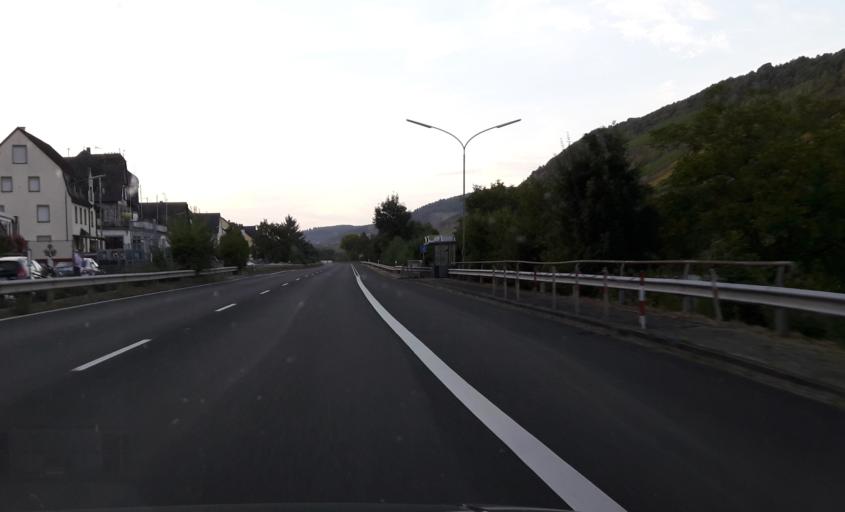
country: DE
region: Rheinland-Pfalz
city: Briedel
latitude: 50.0191
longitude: 7.1520
